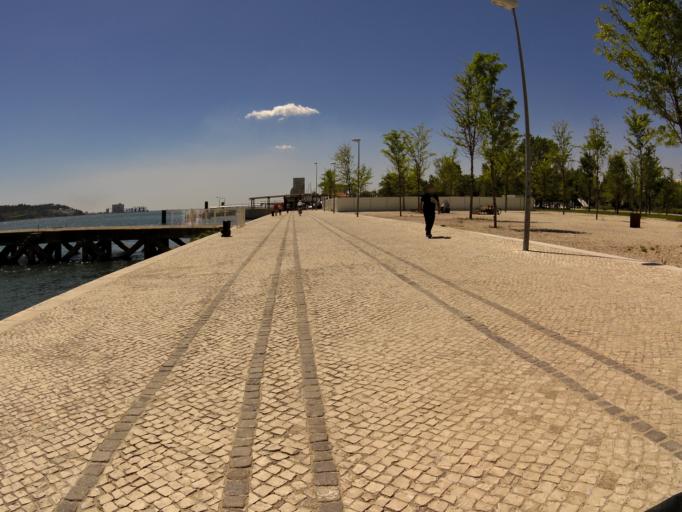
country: PT
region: Setubal
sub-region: Almada
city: Caparica
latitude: 38.6952
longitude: -9.1962
